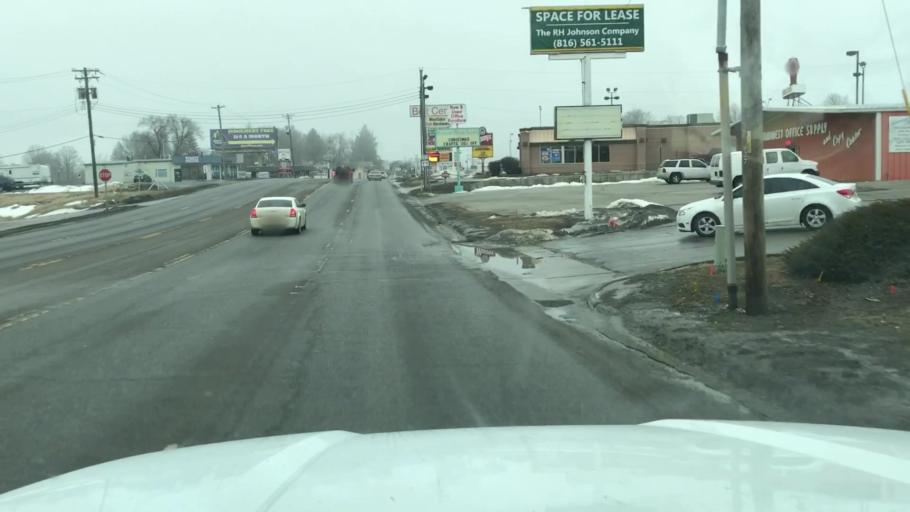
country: US
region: Missouri
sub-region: Buchanan County
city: Saint Joseph
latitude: 39.7529
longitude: -94.8033
